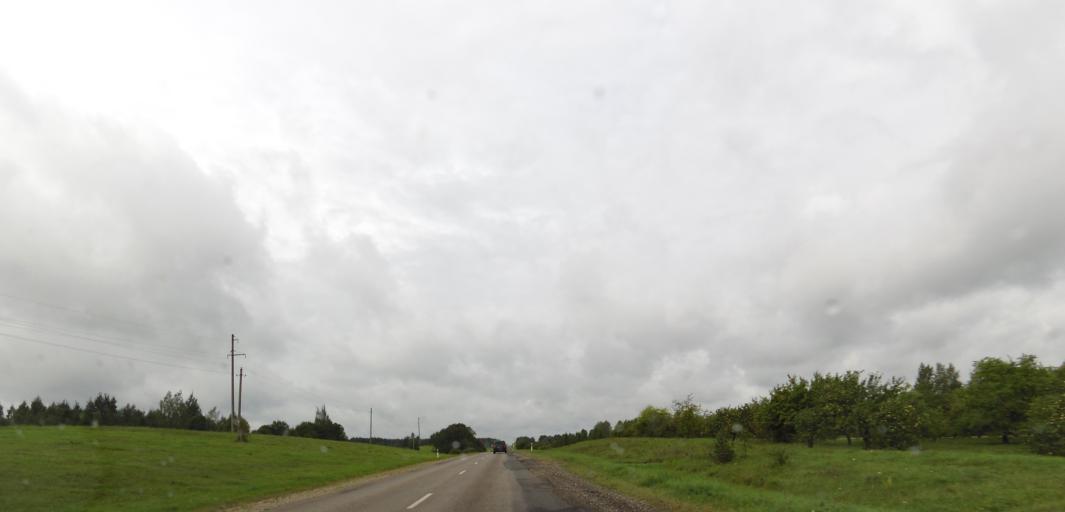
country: LT
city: Moletai
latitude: 55.2129
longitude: 25.2857
